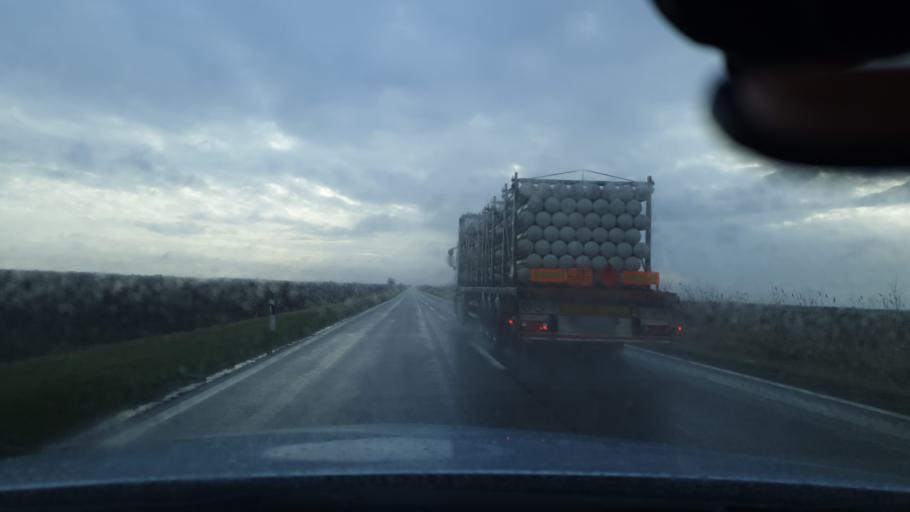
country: RS
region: Autonomna Pokrajina Vojvodina
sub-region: Juznobanatski Okrug
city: Kovin
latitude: 44.7861
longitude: 20.9231
